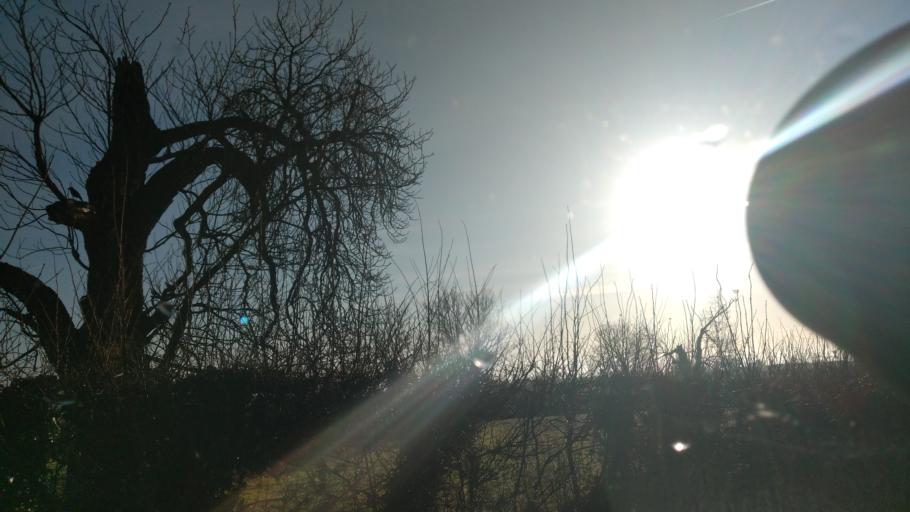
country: GB
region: England
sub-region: Wiltshire
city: Lacock
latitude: 51.4229
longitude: -2.1493
